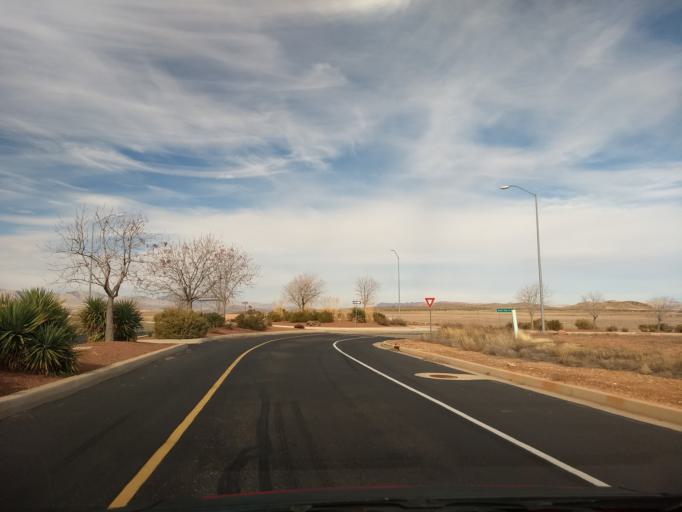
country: US
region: Utah
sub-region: Washington County
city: Washington
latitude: 37.0242
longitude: -113.5078
